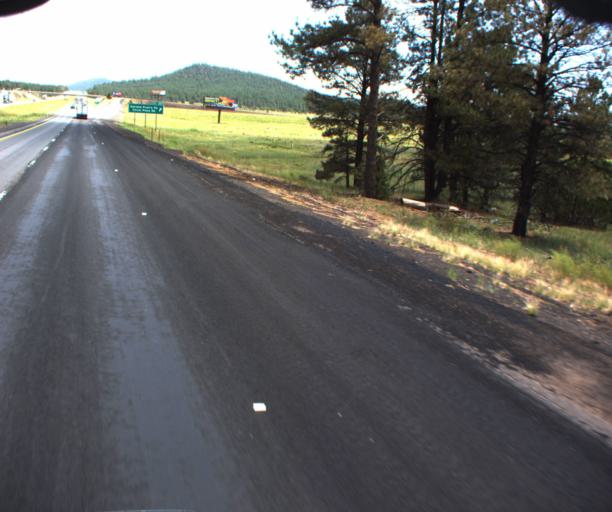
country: US
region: Arizona
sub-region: Coconino County
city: Williams
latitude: 35.2580
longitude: -112.1302
